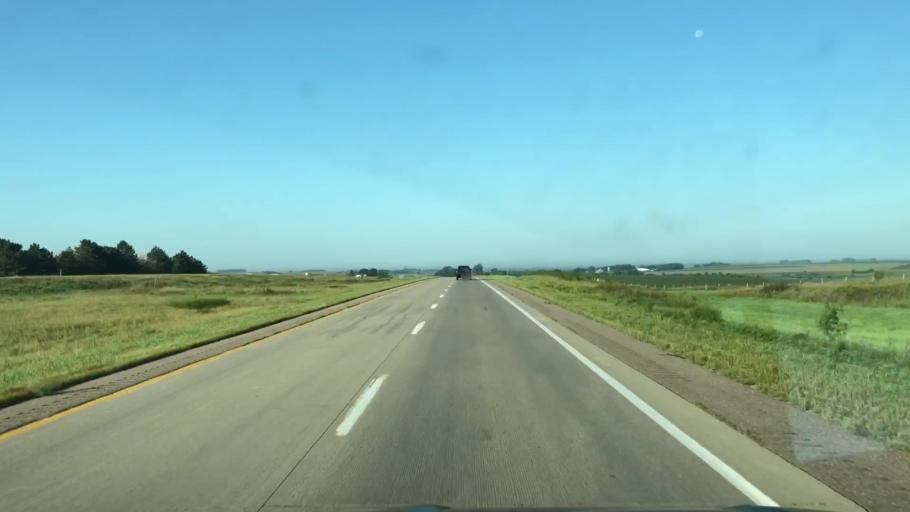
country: US
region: Iowa
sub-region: Sioux County
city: Alton
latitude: 43.0341
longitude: -95.9251
